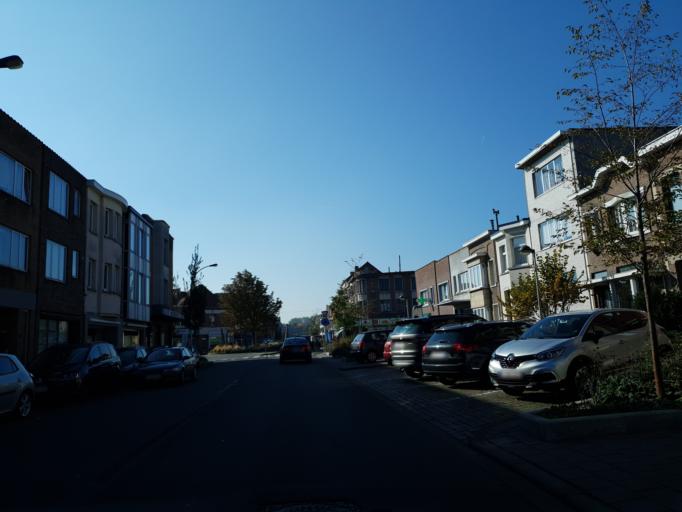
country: BE
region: Flanders
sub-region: Provincie Antwerpen
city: Borsbeek
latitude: 51.2236
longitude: 4.4644
